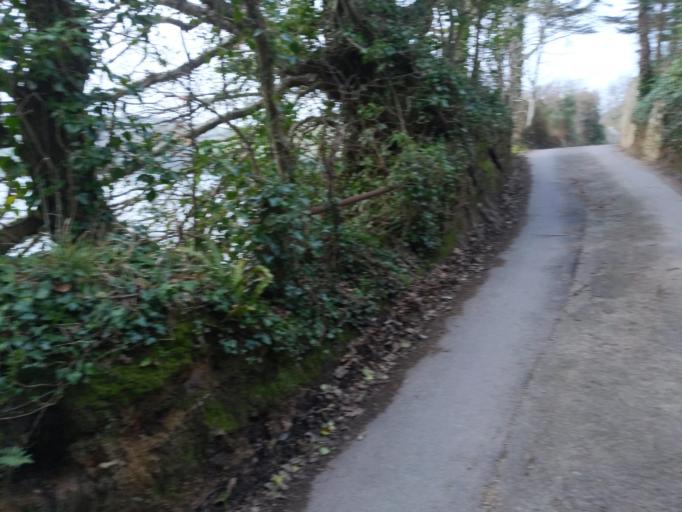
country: GB
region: England
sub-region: Devon
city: Salcombe
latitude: 50.2377
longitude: -3.7448
